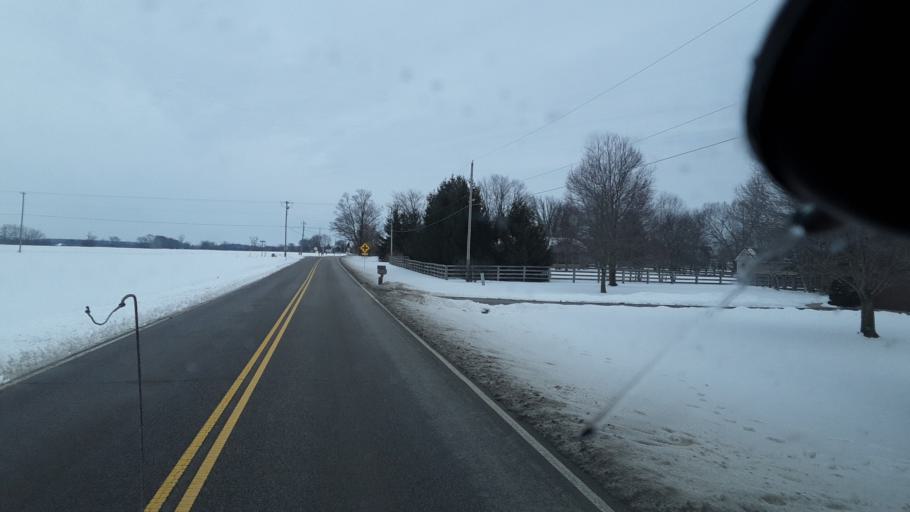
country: US
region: Ohio
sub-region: Union County
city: New California
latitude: 40.2166
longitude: -83.1698
